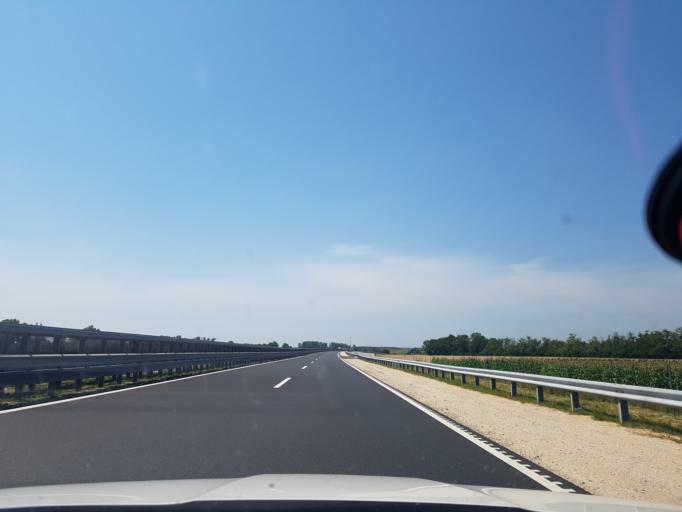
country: HU
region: Vas
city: Sarvar
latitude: 47.3382
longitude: 16.8837
